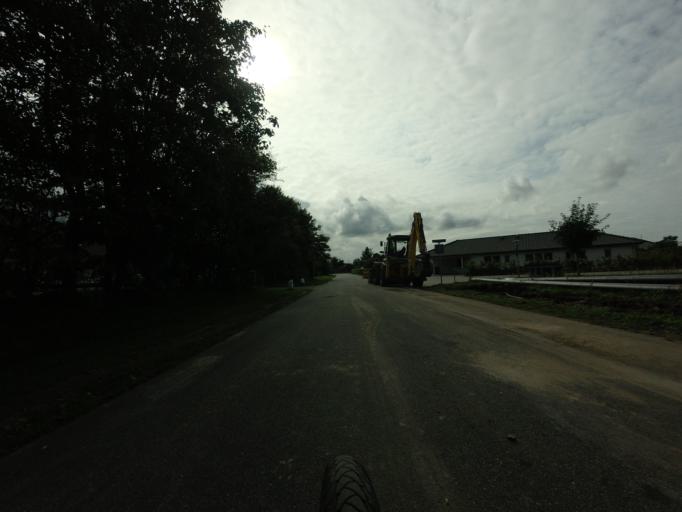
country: DK
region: North Denmark
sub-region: Hjorring Kommune
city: Hjorring
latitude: 57.4870
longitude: 9.9944
